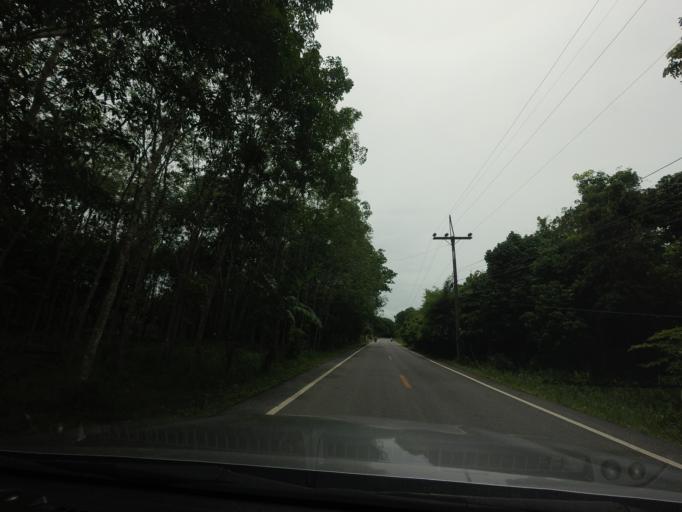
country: TH
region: Pattani
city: Kapho
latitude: 6.6226
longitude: 101.5443
